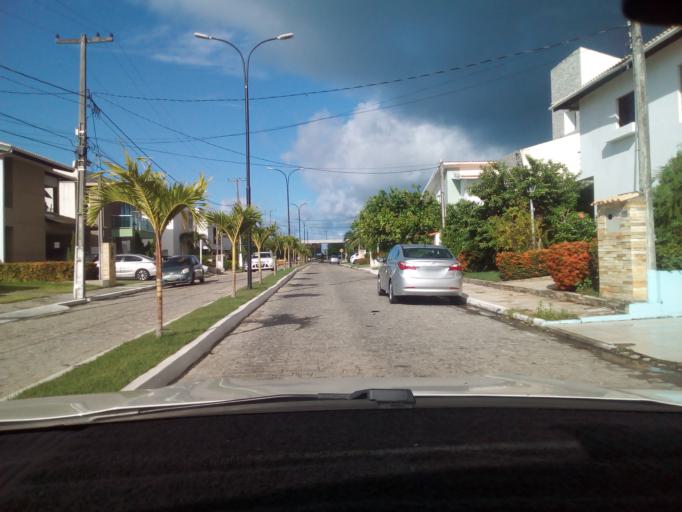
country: BR
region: Paraiba
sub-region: Joao Pessoa
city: Joao Pessoa
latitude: -7.1404
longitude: -34.8208
